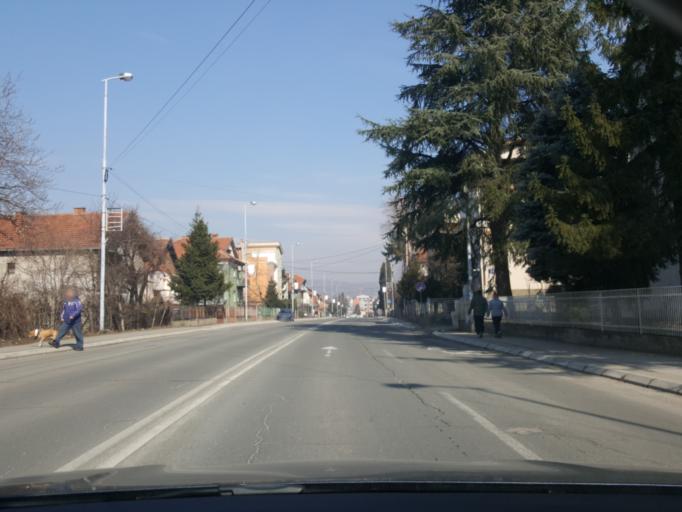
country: RS
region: Central Serbia
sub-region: Nisavski Okrug
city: Nis
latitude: 43.3260
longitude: 21.9254
